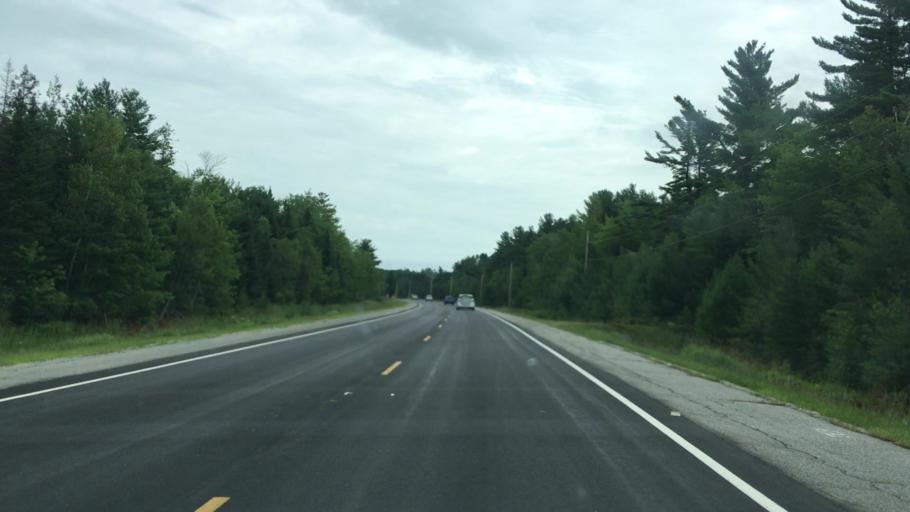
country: US
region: Maine
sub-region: Washington County
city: Addison
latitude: 44.9406
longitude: -67.7177
